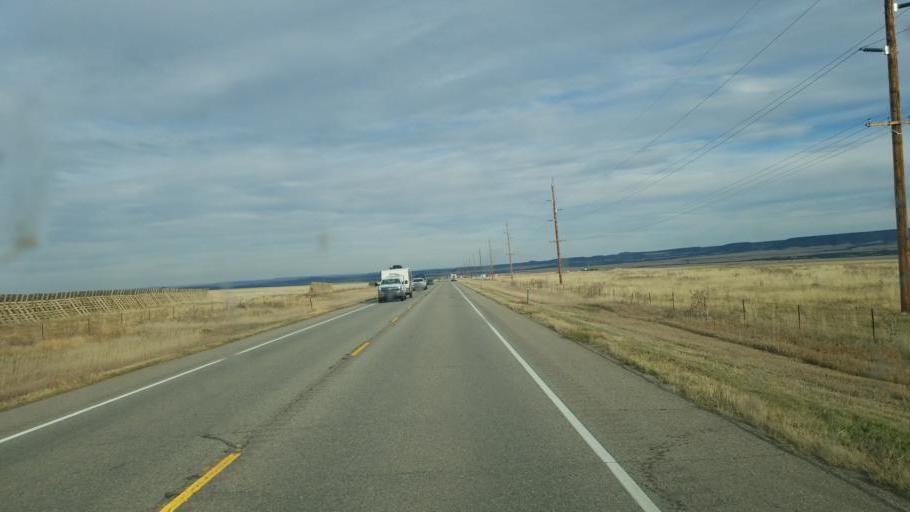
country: US
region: Colorado
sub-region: Huerfano County
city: Walsenburg
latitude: 37.5420
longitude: -105.0506
